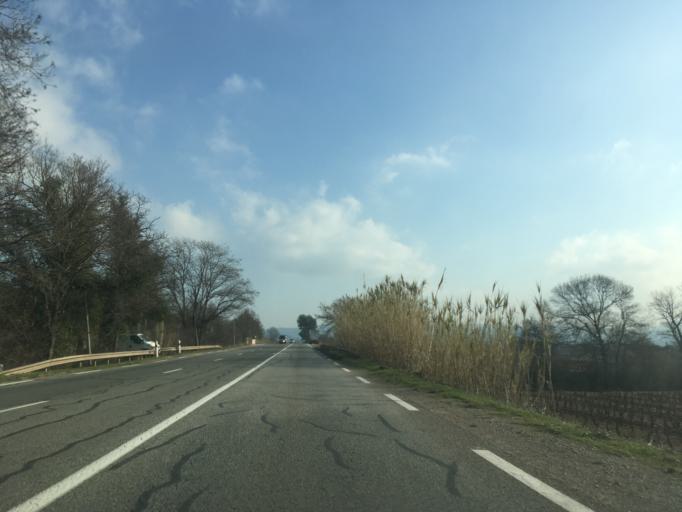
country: FR
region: Provence-Alpes-Cote d'Azur
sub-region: Departement du Var
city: Vidauban
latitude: 43.4050
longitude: 6.4034
